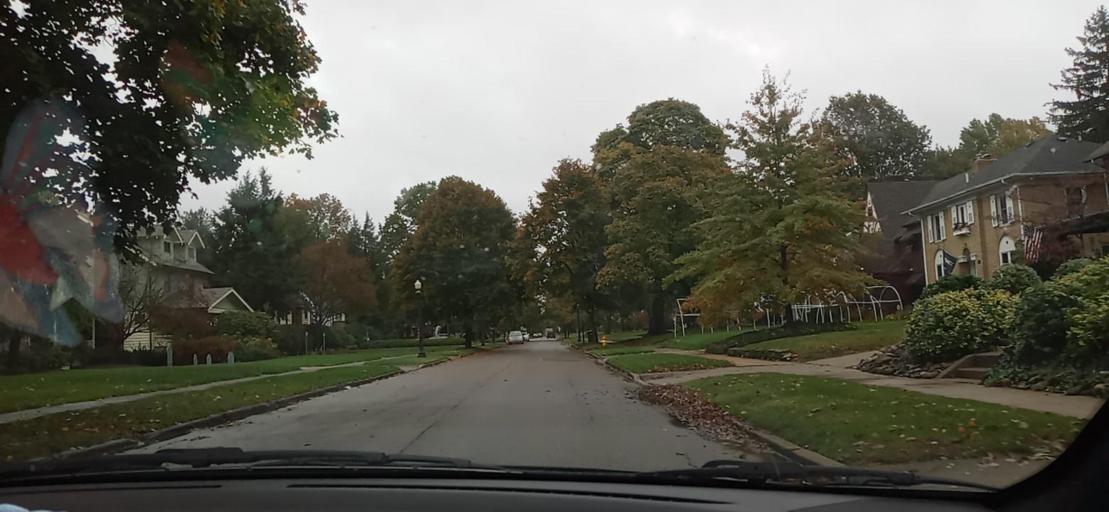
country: US
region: Ohio
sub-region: Summit County
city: Akron
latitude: 41.1096
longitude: -81.5599
